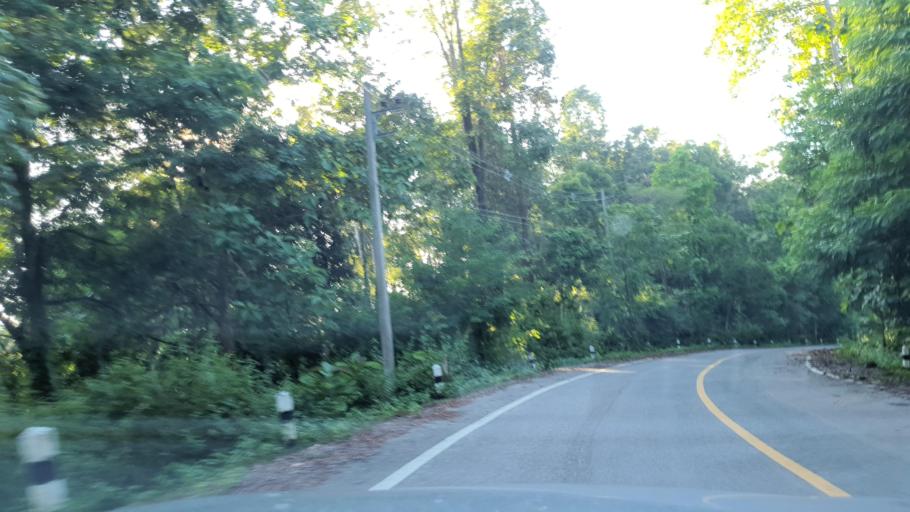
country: TH
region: Chiang Mai
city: Mae On
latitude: 18.8093
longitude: 99.3002
